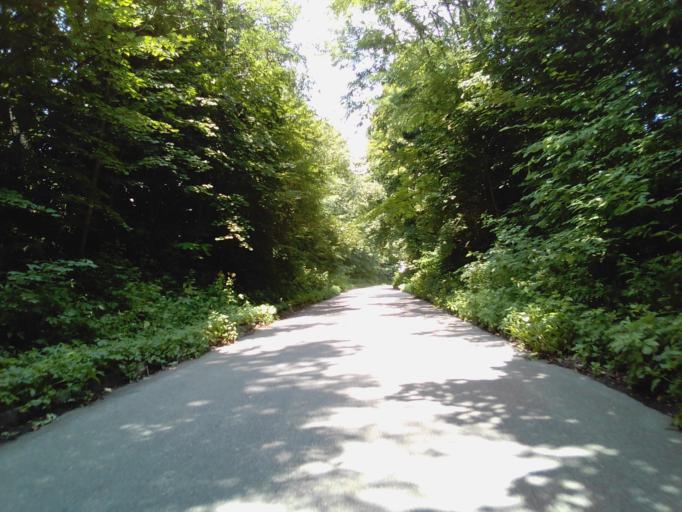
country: PL
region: Subcarpathian Voivodeship
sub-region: Powiat strzyzowski
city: Frysztak
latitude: 49.8060
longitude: 21.5833
